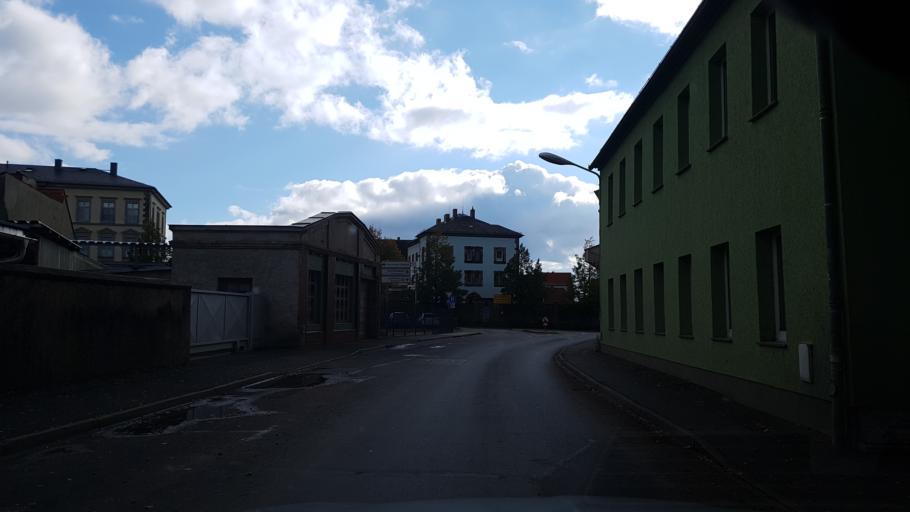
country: DE
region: Saxony
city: Grossenhain
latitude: 51.2896
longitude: 13.5255
